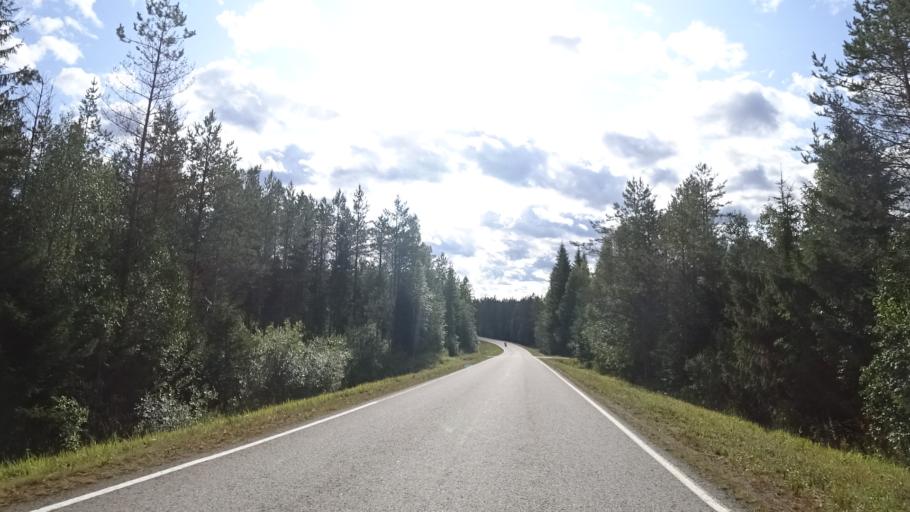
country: RU
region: Republic of Karelia
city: Vyartsilya
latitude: 62.2371
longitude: 30.6937
